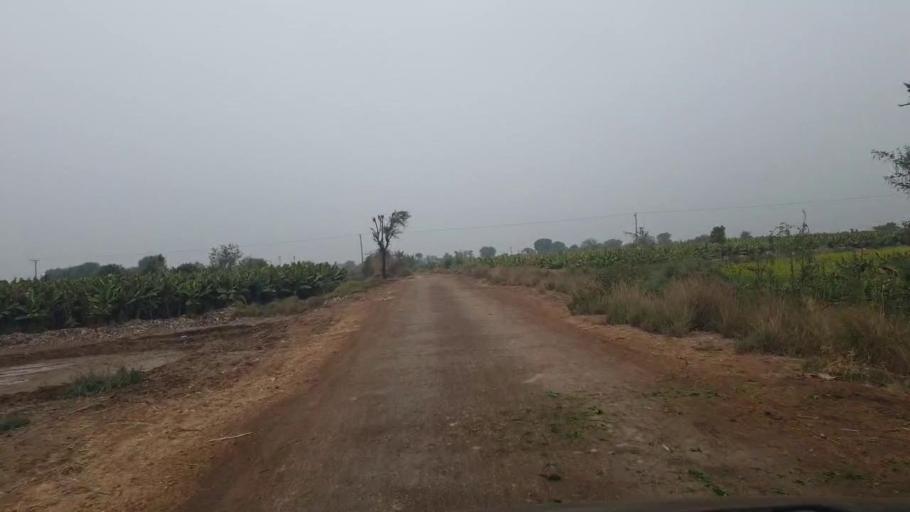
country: PK
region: Sindh
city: Tando Adam
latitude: 25.8314
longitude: 68.6791
